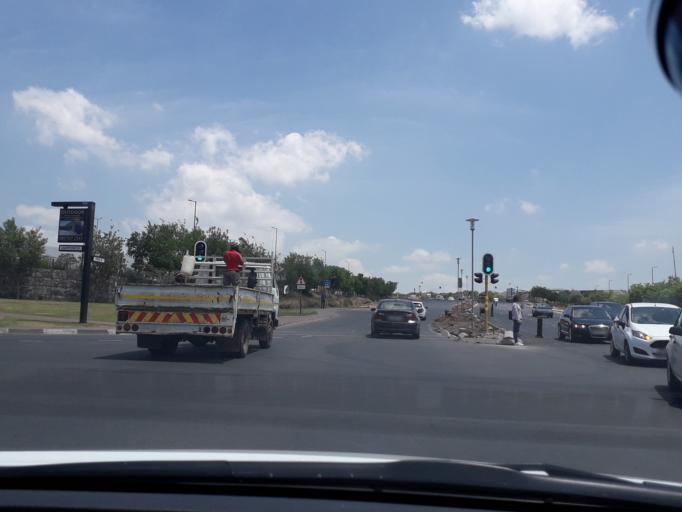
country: ZA
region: Gauteng
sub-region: City of Johannesburg Metropolitan Municipality
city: Midrand
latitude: -26.0204
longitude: 28.0903
